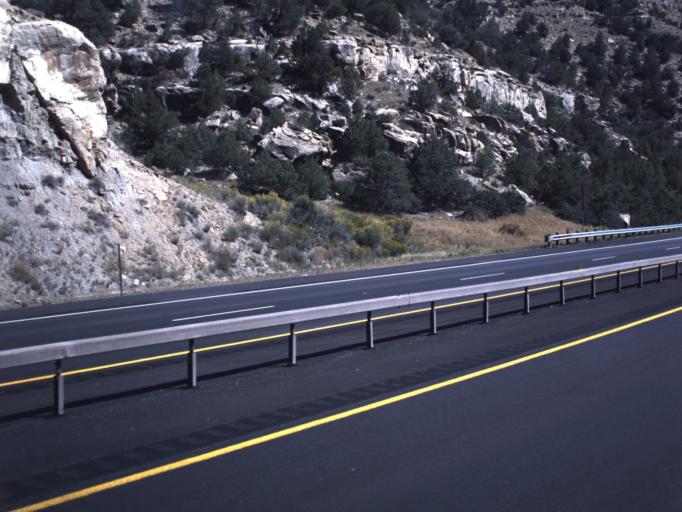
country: US
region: Utah
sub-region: Sevier County
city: Salina
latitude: 38.8844
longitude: -111.6011
